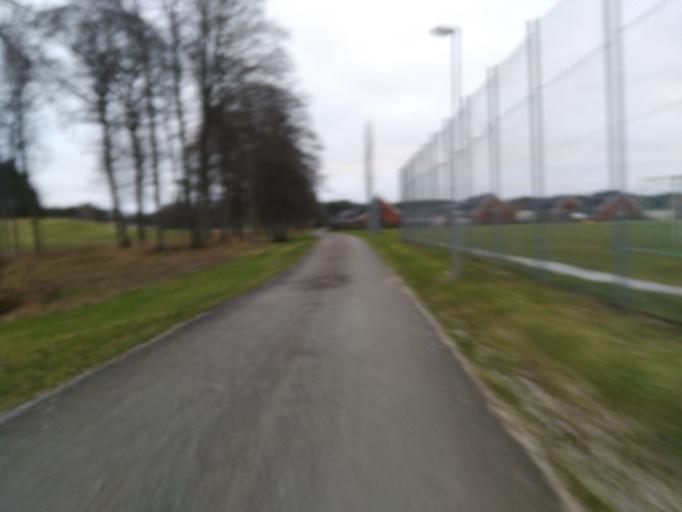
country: SE
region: Vaestra Goetaland
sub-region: Lidkopings Kommun
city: Lidkoping
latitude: 58.4930
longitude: 13.1751
